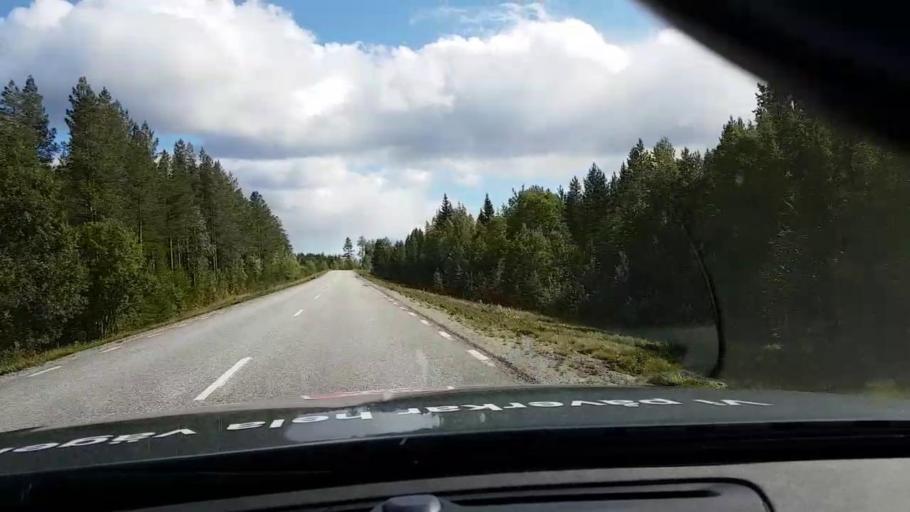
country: SE
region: Vaesterbotten
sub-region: Asele Kommun
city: Asele
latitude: 63.7741
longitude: 17.6754
